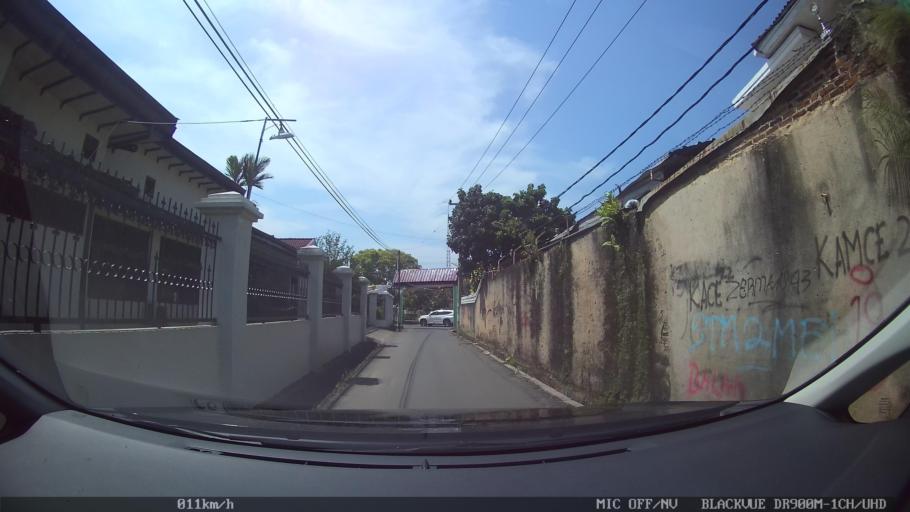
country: ID
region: Lampung
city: Kedaton
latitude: -5.3815
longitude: 105.2668
